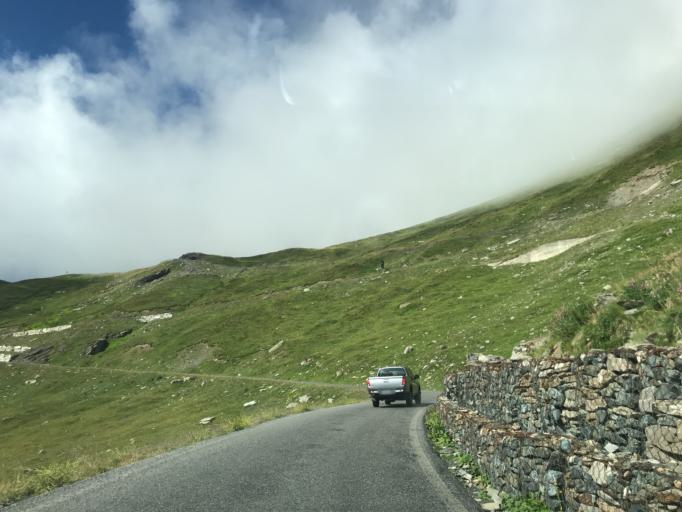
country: IT
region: Piedmont
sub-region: Provincia di Cuneo
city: Pontechianale
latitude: 44.6725
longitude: 6.9909
